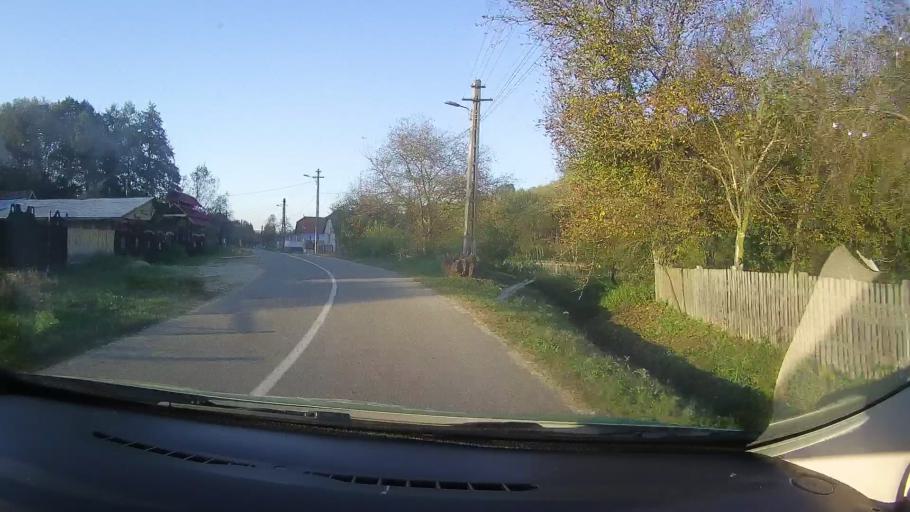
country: RO
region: Timis
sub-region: Comuna Fardea
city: Fardea
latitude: 45.7101
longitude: 22.1599
